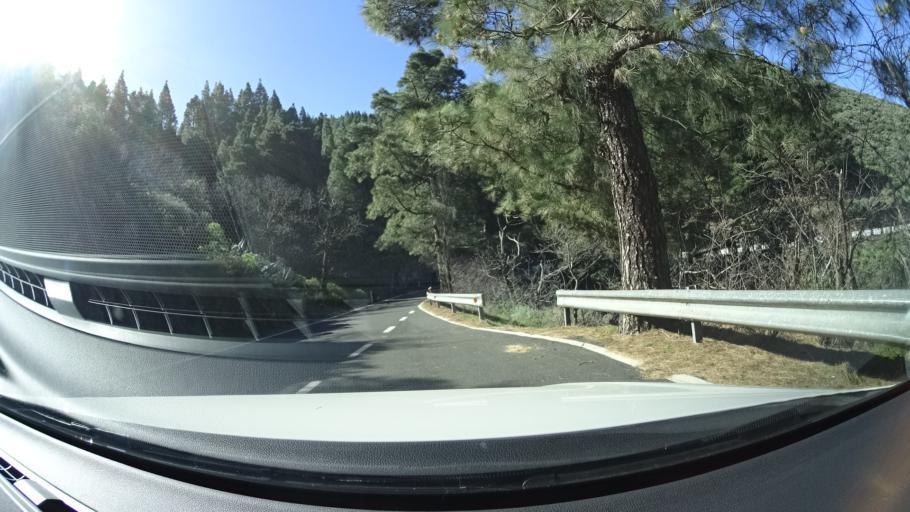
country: ES
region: Canary Islands
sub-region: Provincia de Las Palmas
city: Artenara
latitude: 28.0265
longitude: -15.6179
